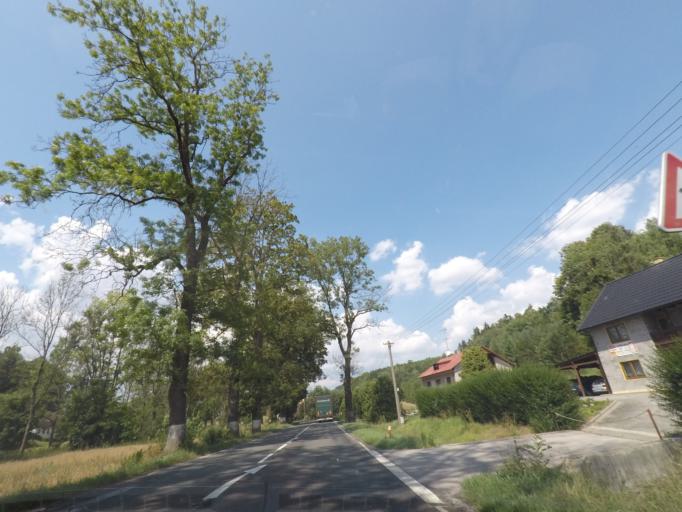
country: CZ
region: Kralovehradecky
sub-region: Okres Trutnov
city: Hostinne
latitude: 50.5210
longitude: 15.7240
